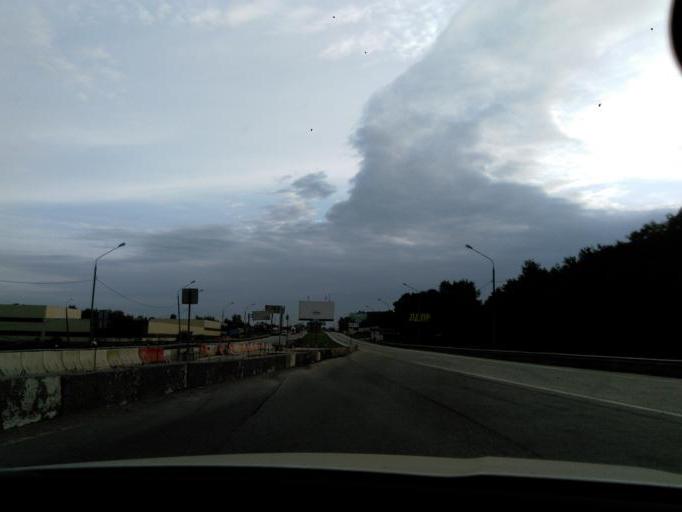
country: RU
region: Moskovskaya
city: Novopodrezkovo
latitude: 55.9725
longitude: 37.3776
